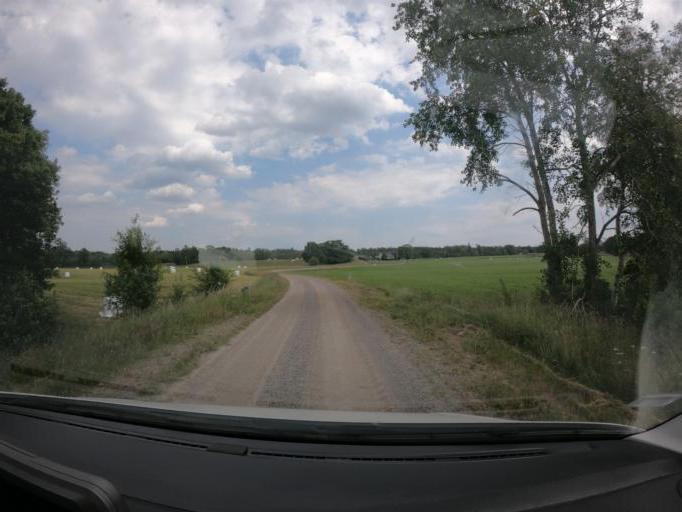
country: SE
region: Skane
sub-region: Perstorps Kommun
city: Perstorp
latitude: 56.2372
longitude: 13.5347
